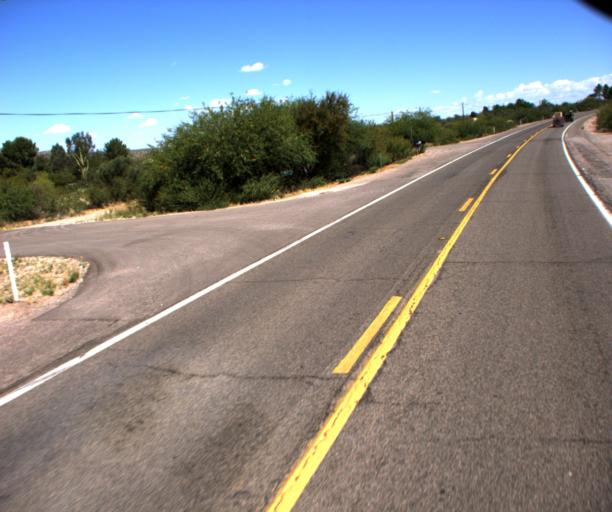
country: US
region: Arizona
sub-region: Pinal County
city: Mammoth
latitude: 32.8406
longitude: -110.7111
